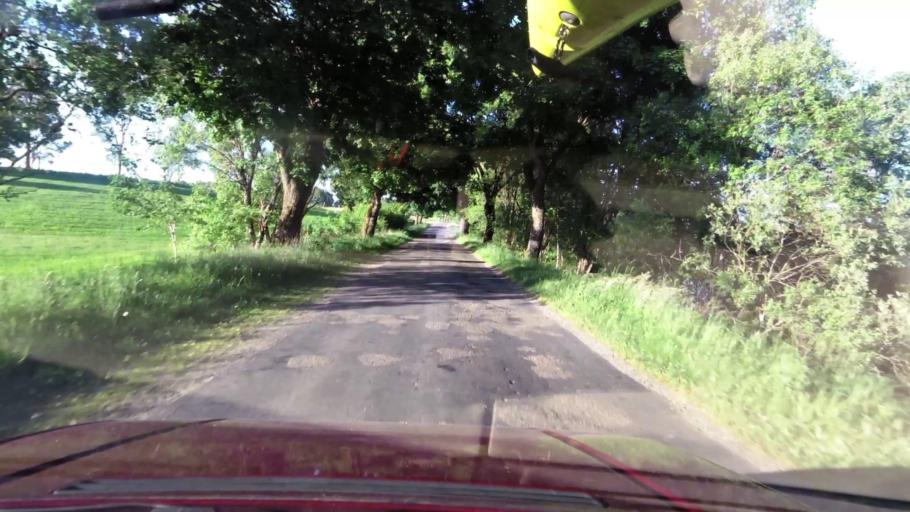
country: PL
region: West Pomeranian Voivodeship
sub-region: Powiat szczecinecki
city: Bialy Bor
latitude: 53.9451
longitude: 16.7693
